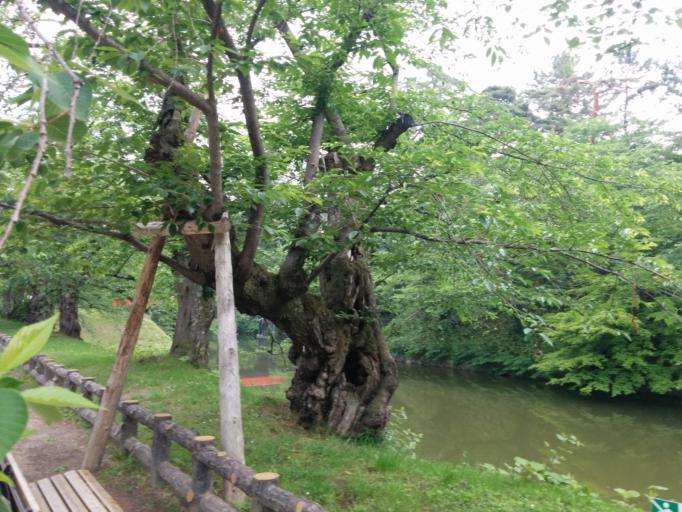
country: JP
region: Aomori
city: Hirosaki
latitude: 40.6054
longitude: 140.4645
